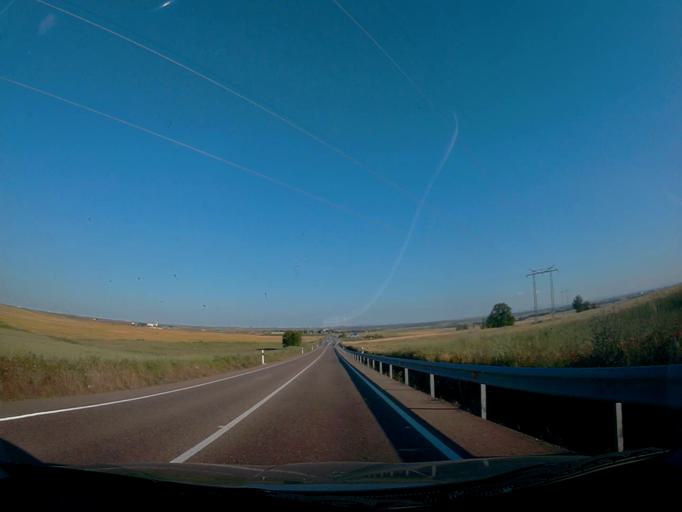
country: ES
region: Castille-La Mancha
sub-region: Province of Toledo
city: Maqueda
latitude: 40.0830
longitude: -4.3821
